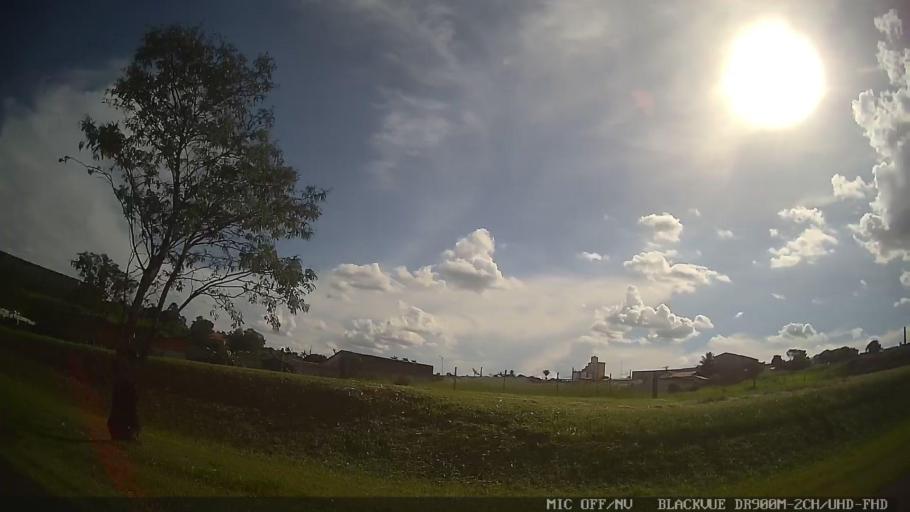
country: BR
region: Sao Paulo
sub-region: Laranjal Paulista
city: Laranjal Paulista
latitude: -23.0412
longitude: -47.8290
